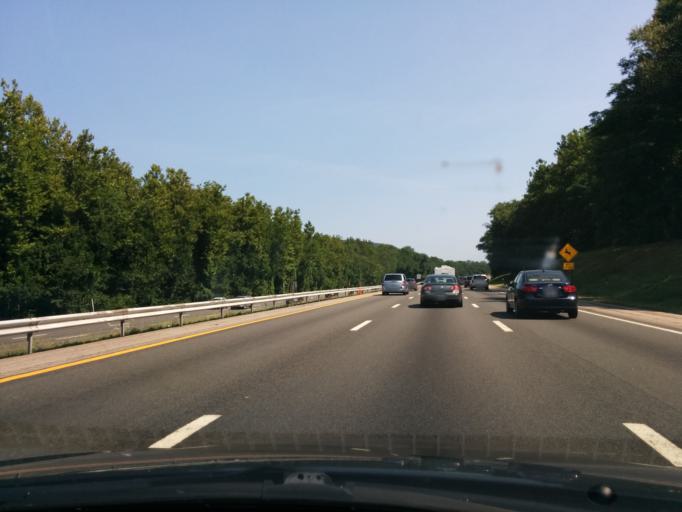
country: US
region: New York
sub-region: Orange County
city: Harriman
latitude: 41.2456
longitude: -74.1694
